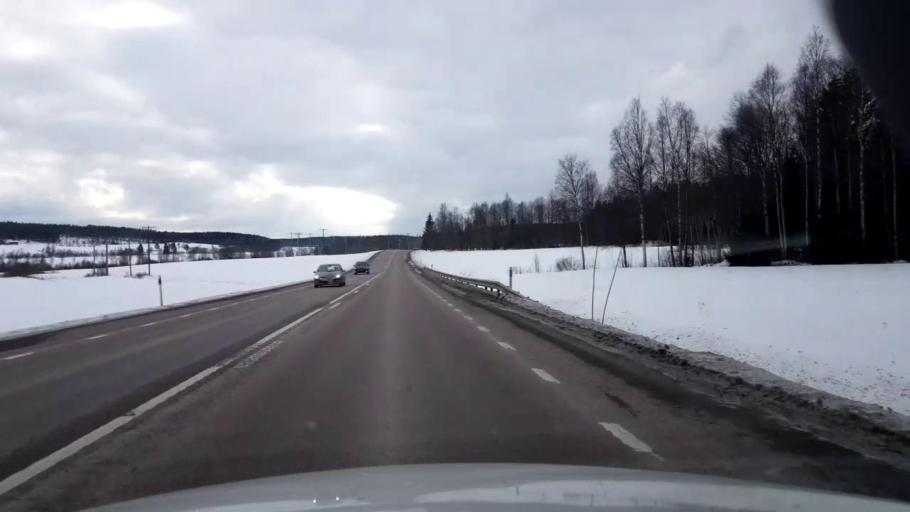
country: SE
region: Gaevleborg
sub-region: Nordanstigs Kommun
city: Bergsjoe
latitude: 62.0200
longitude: 17.2518
